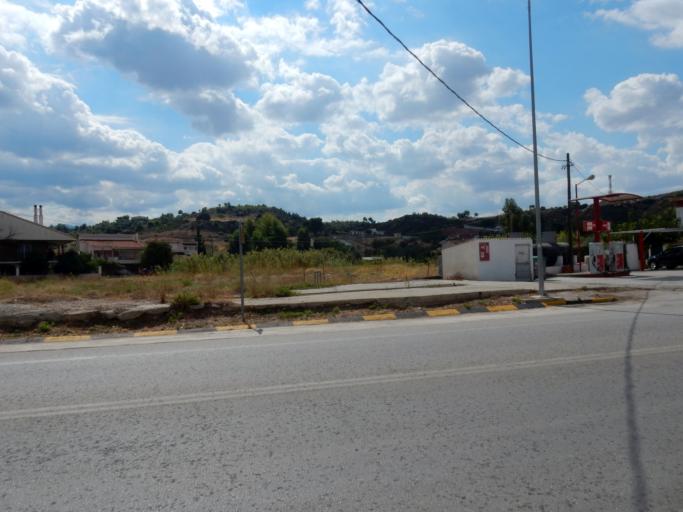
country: GR
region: Attica
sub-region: Nomarchia Anatolikis Attikis
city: Khalkoutsion
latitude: 38.3292
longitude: 23.7419
